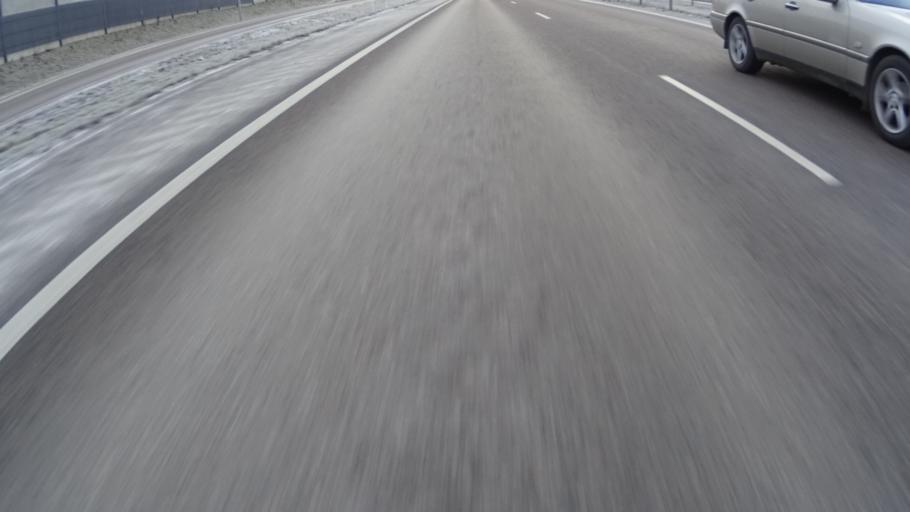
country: FI
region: Uusimaa
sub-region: Helsinki
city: Kilo
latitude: 60.3180
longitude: 24.8363
